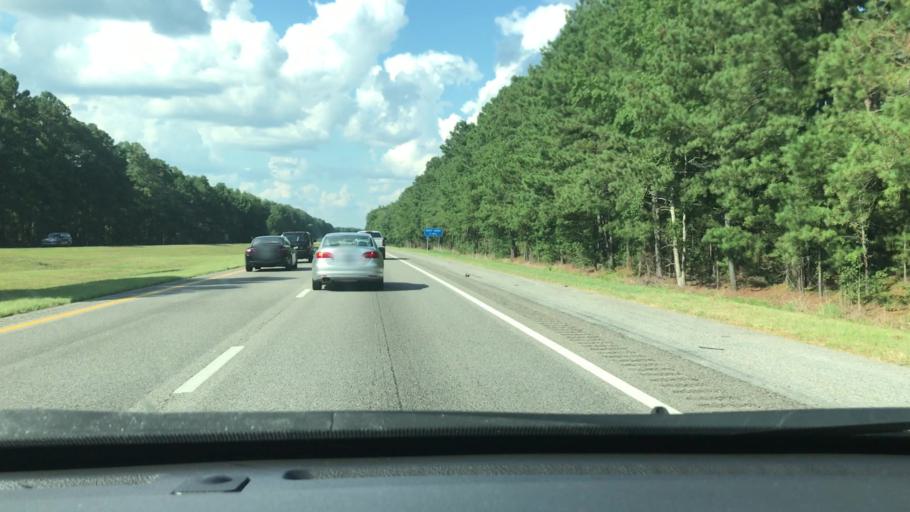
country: US
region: South Carolina
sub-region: Sumter County
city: East Sumter
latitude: 33.9313
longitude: -80.0688
